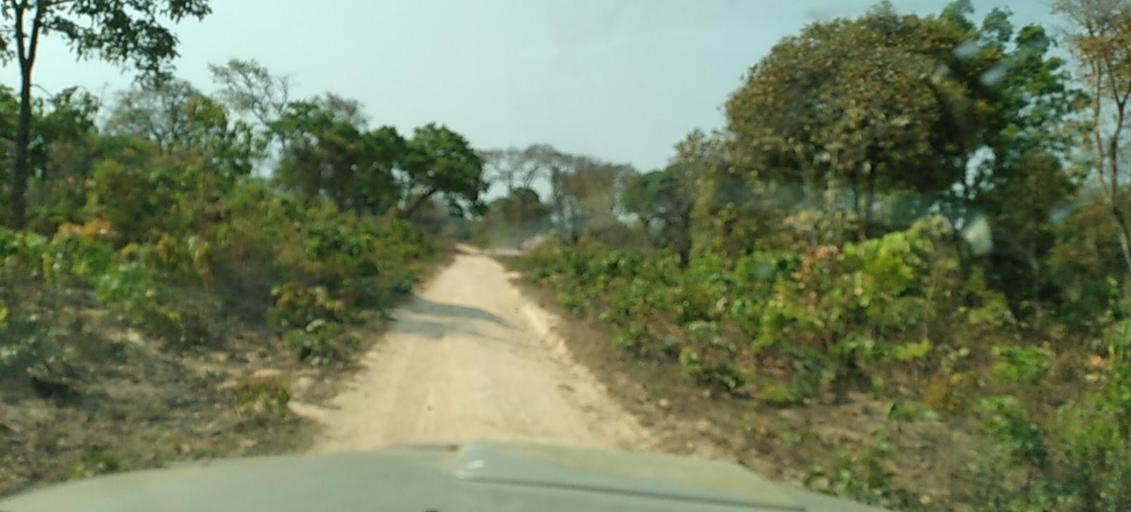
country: ZM
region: North-Western
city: Kasempa
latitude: -13.5436
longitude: 26.4088
